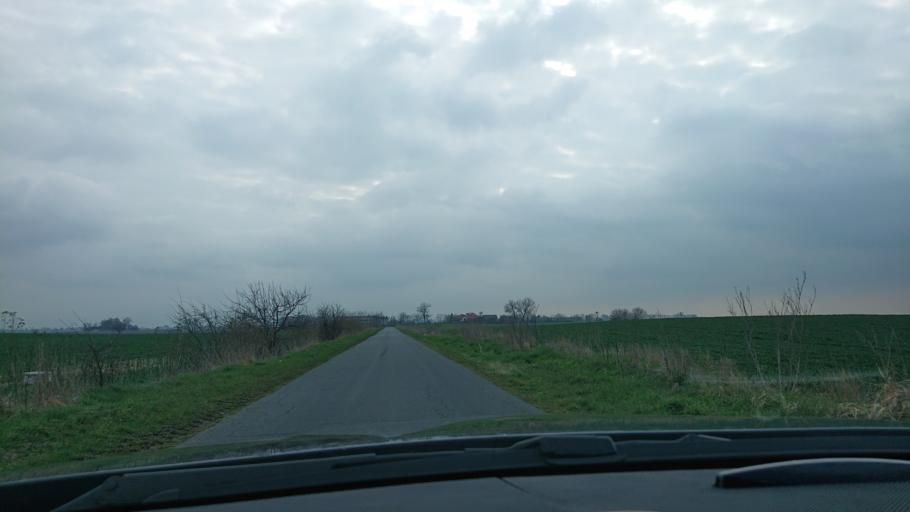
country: PL
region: Greater Poland Voivodeship
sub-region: Powiat gnieznienski
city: Gniezno
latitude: 52.5578
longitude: 17.5143
